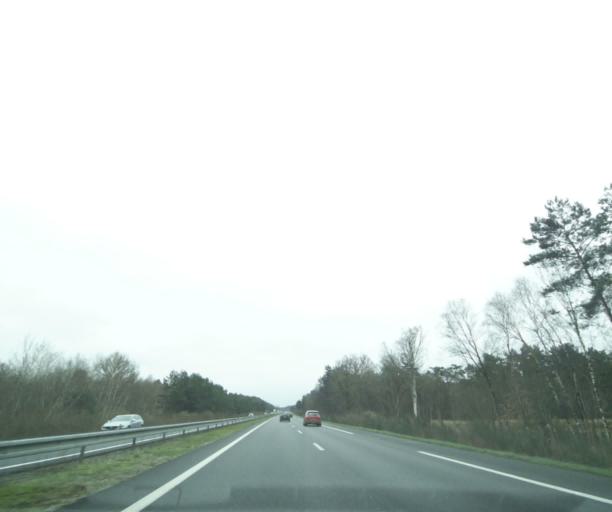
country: FR
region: Centre
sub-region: Departement du Loir-et-Cher
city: Chaumont-sur-Tharonne
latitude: 47.6595
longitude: 1.9320
